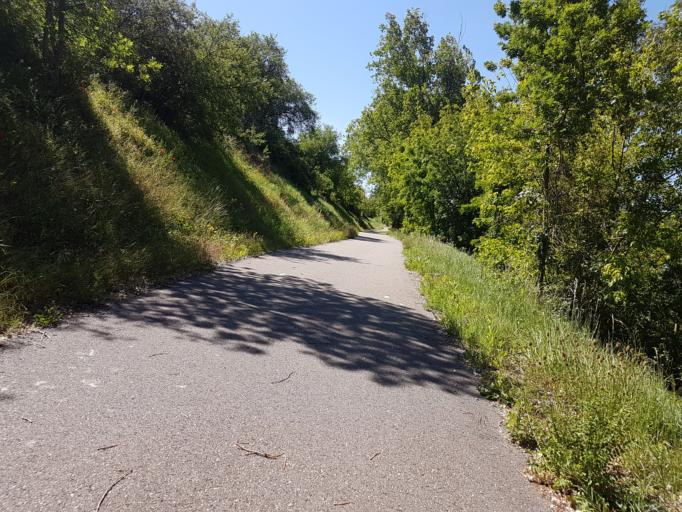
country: FR
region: Rhone-Alpes
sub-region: Departement de la Drome
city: Andancette
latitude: 45.2763
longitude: 4.8113
